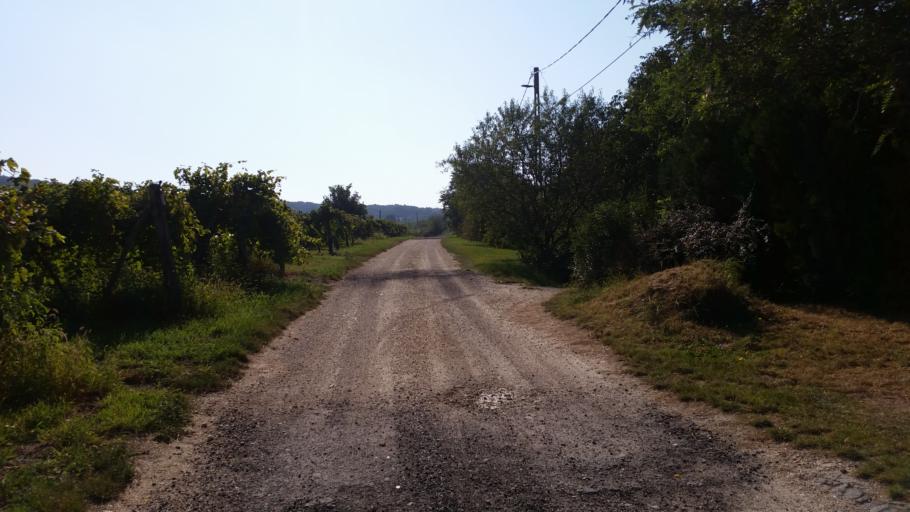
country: HU
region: Pest
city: Telki
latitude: 47.5480
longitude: 18.8343
